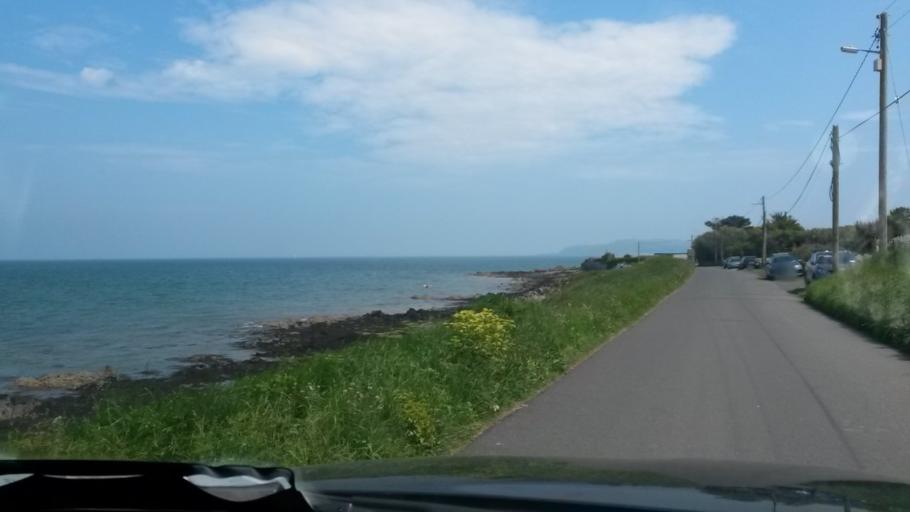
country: IE
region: Leinster
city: Portraine
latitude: 53.4929
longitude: -6.1034
